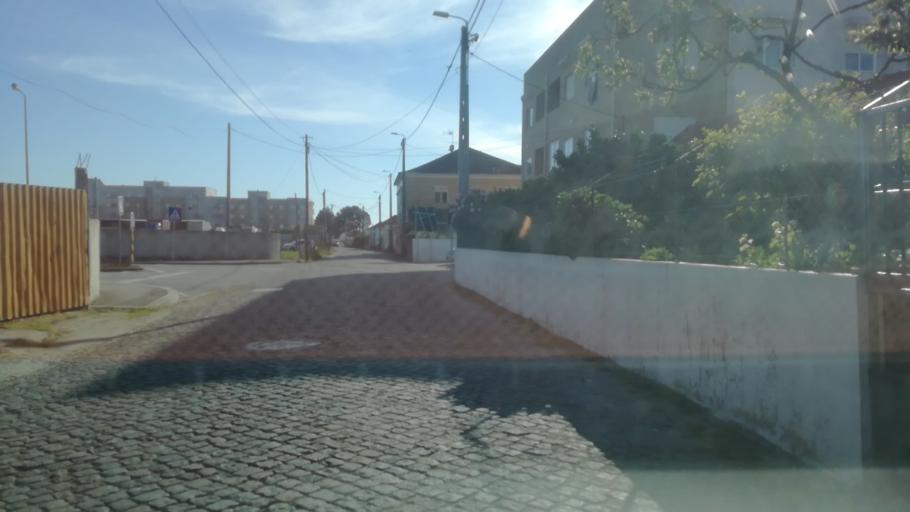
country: PT
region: Porto
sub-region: Matosinhos
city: Santa Cruz do Bispo
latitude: 41.2499
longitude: -8.6728
